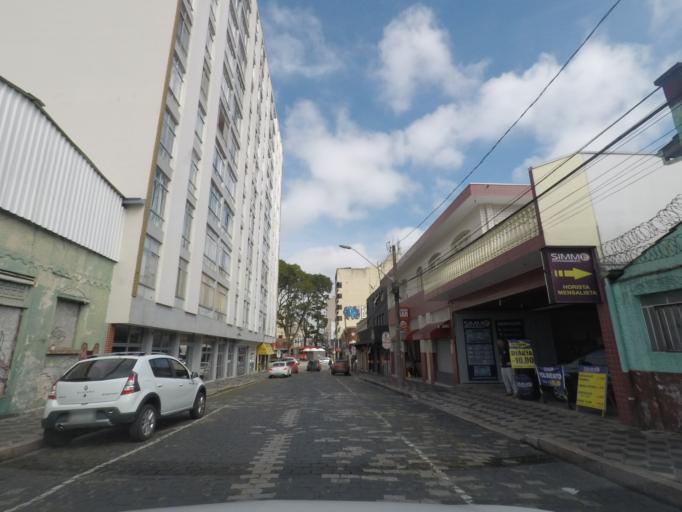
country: BR
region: Parana
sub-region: Curitiba
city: Curitiba
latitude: -25.4309
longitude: -49.2781
